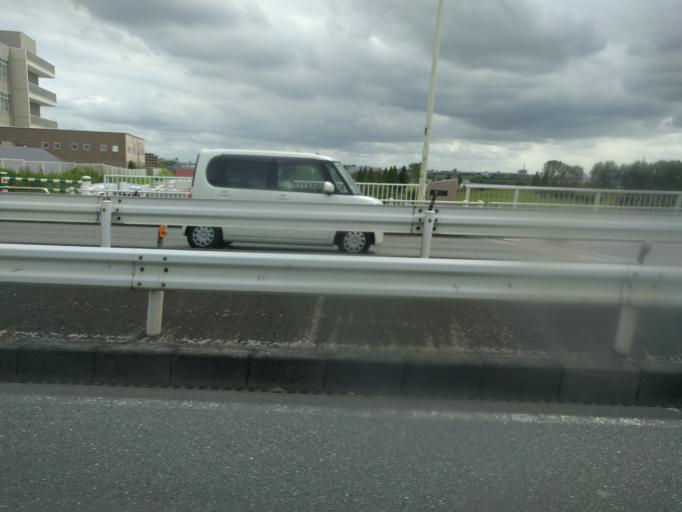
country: JP
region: Saitama
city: Kawaguchi
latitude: 35.7928
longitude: 139.7251
